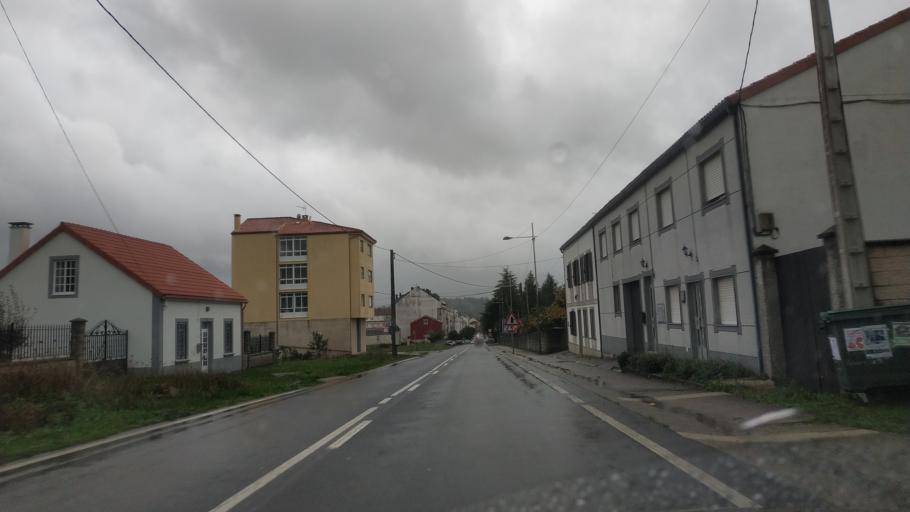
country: ES
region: Galicia
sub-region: Provincia da Coruna
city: Negreira
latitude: 42.9179
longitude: -8.7342
